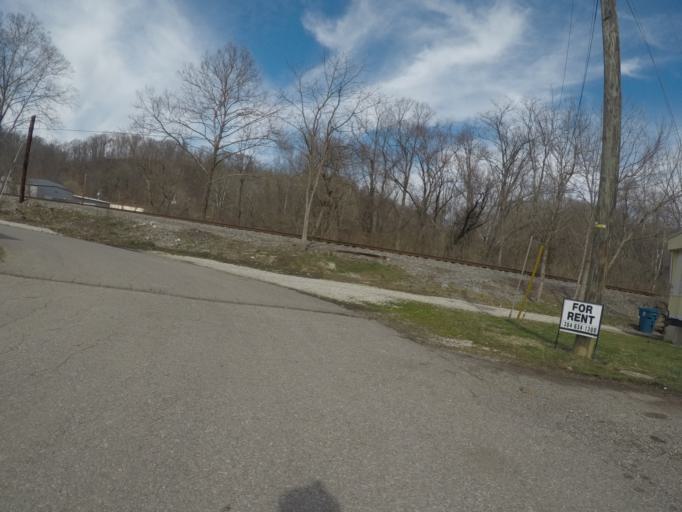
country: US
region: West Virginia
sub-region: Cabell County
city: Pea Ridge
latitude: 38.4195
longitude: -82.3458
